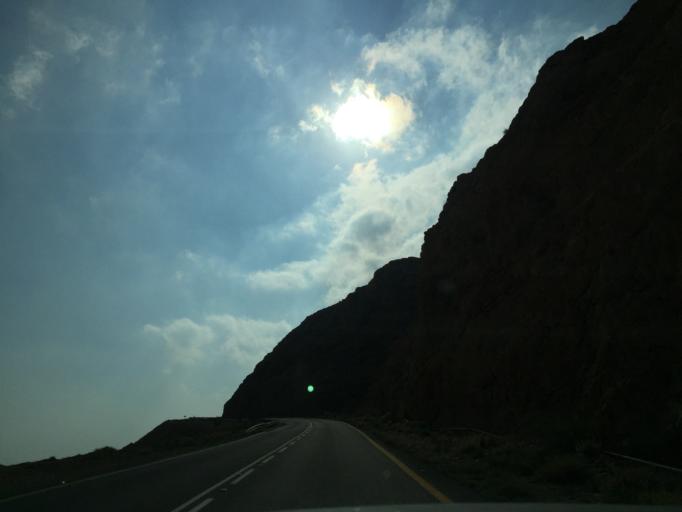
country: IL
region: Southern District
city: `En Boqeq
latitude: 31.3226
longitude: 35.3329
